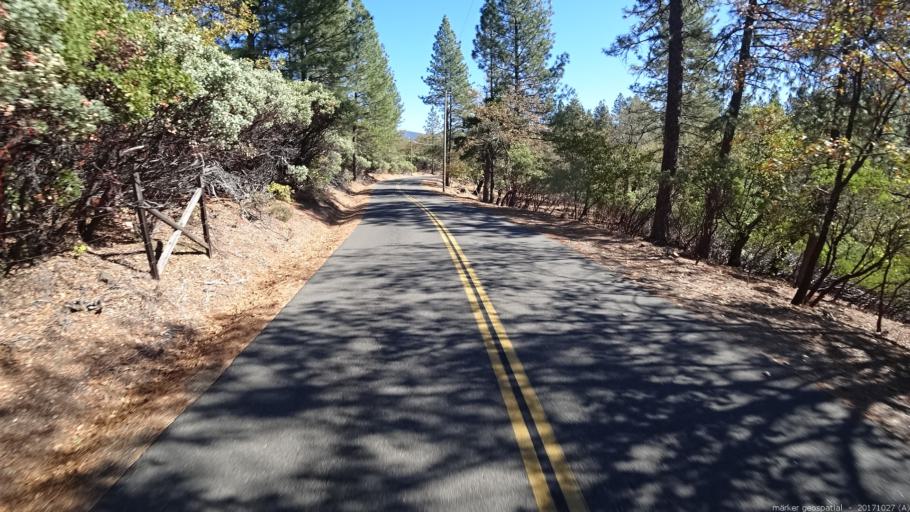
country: US
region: California
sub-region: Shasta County
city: Shingletown
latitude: 40.7528
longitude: -121.9634
